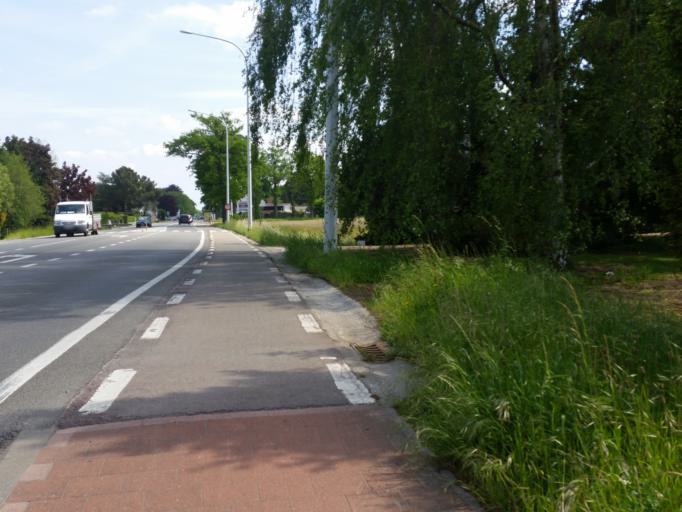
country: BE
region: Flanders
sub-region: Provincie Antwerpen
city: Bonheiden
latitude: 50.9990
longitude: 4.5250
